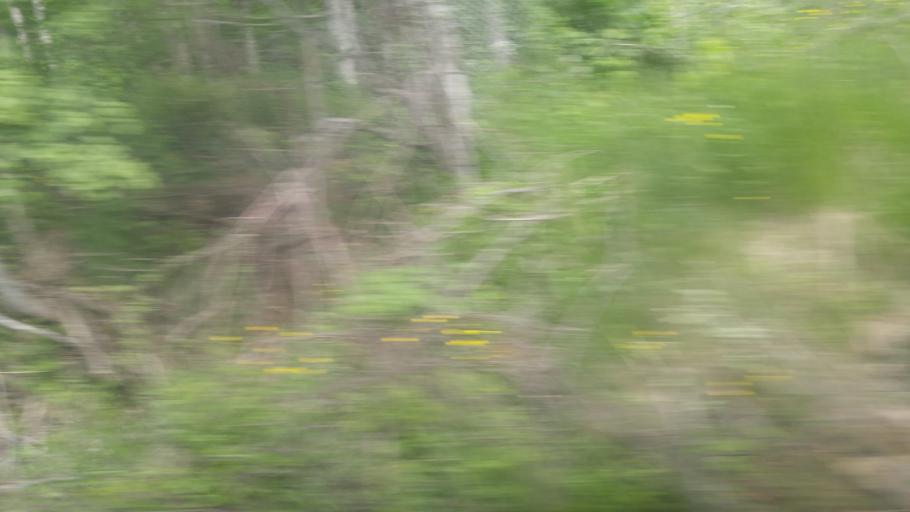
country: NO
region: Sor-Trondelag
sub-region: Midtre Gauldal
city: Storen
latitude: 62.9432
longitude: 10.6473
